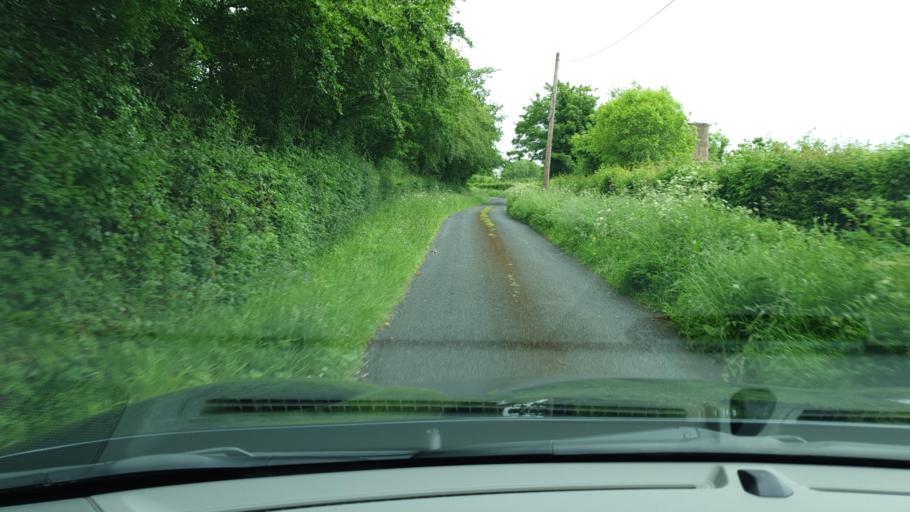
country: IE
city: Confey
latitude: 53.4214
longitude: -6.5295
